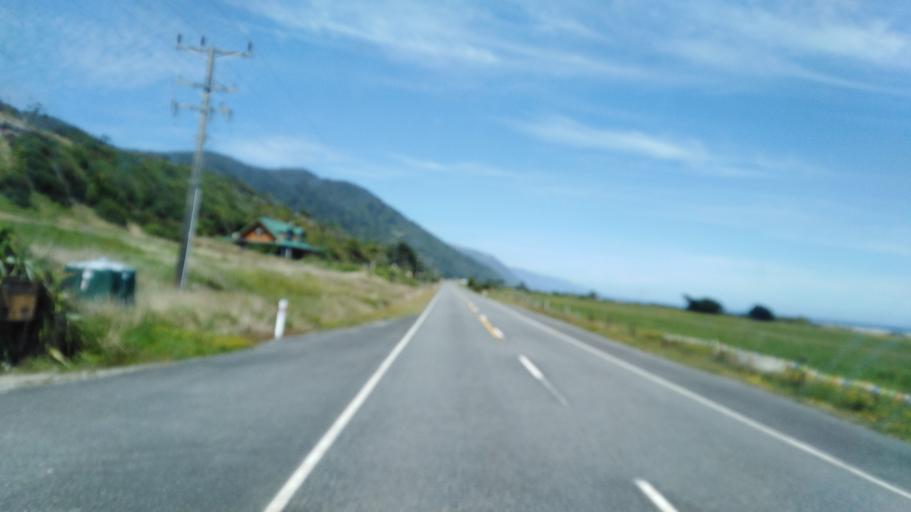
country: NZ
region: West Coast
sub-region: Buller District
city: Westport
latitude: -41.5463
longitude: 171.9251
